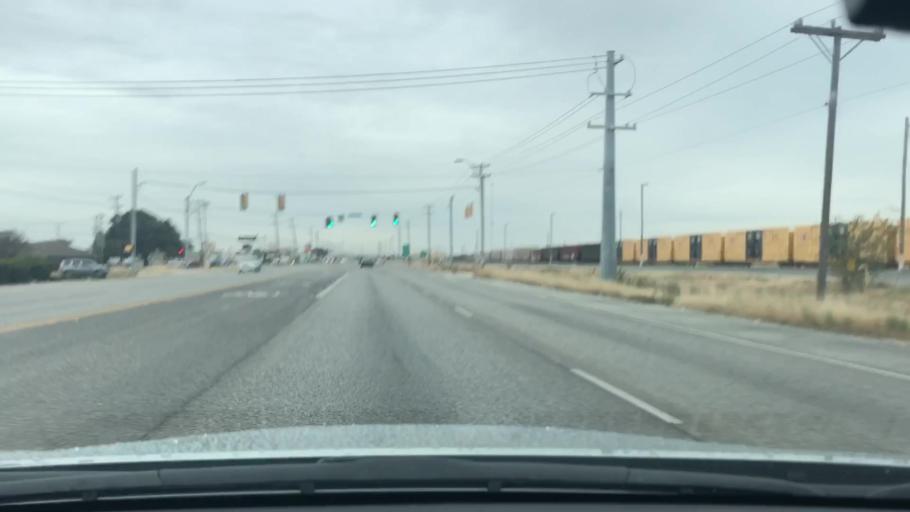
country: US
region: Texas
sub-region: Bexar County
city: Kirby
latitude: 29.4646
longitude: -98.3970
